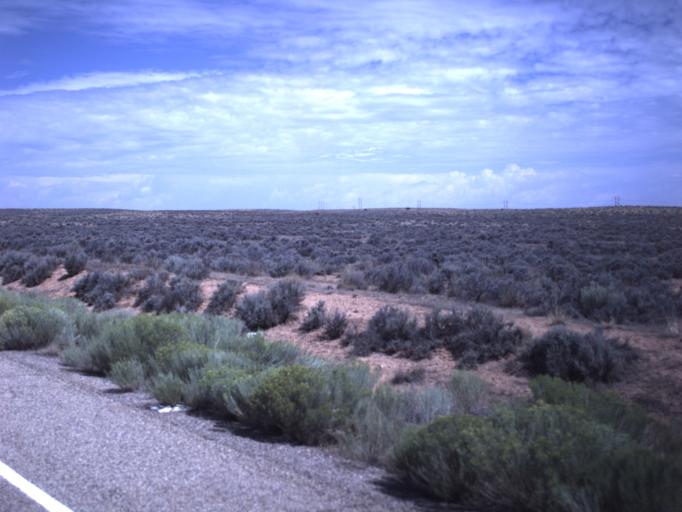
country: US
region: Utah
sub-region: Uintah County
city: Naples
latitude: 40.1454
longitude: -109.2888
